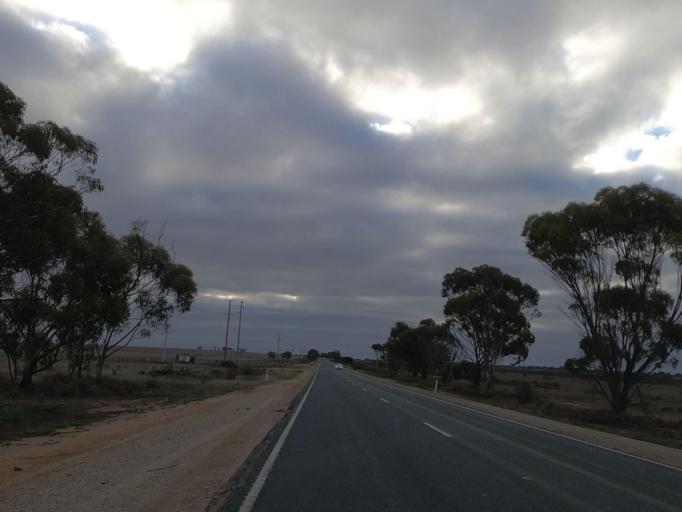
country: AU
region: Victoria
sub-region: Swan Hill
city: Swan Hill
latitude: -35.6397
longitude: 143.8277
